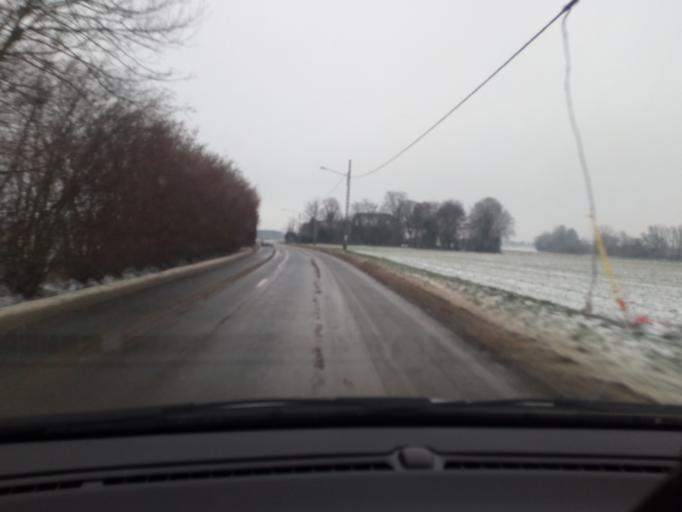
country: FR
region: Nord-Pas-de-Calais
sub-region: Departement du Nord
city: La Longueville
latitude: 50.3431
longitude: 3.8780
